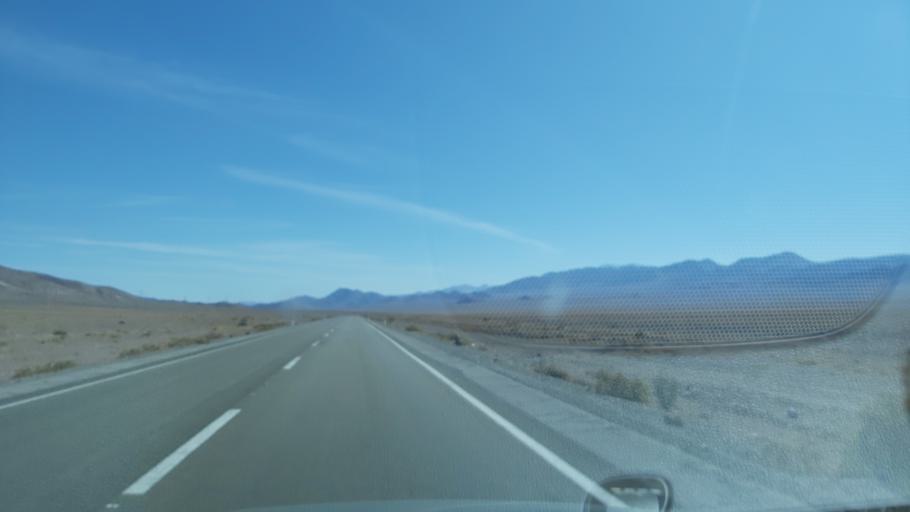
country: CL
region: Atacama
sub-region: Provincia de Chanaral
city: Diego de Almagro
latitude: -26.8732
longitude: -69.9097
